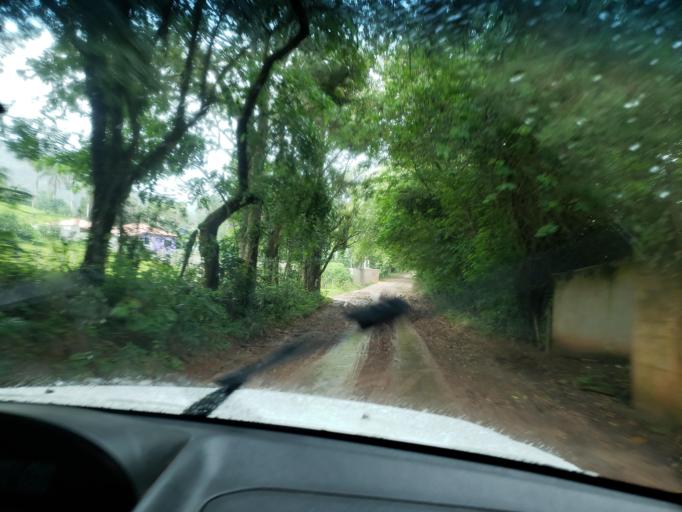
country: BR
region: Minas Gerais
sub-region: Monte Siao
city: Monte Siao
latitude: -22.3797
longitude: -46.5581
